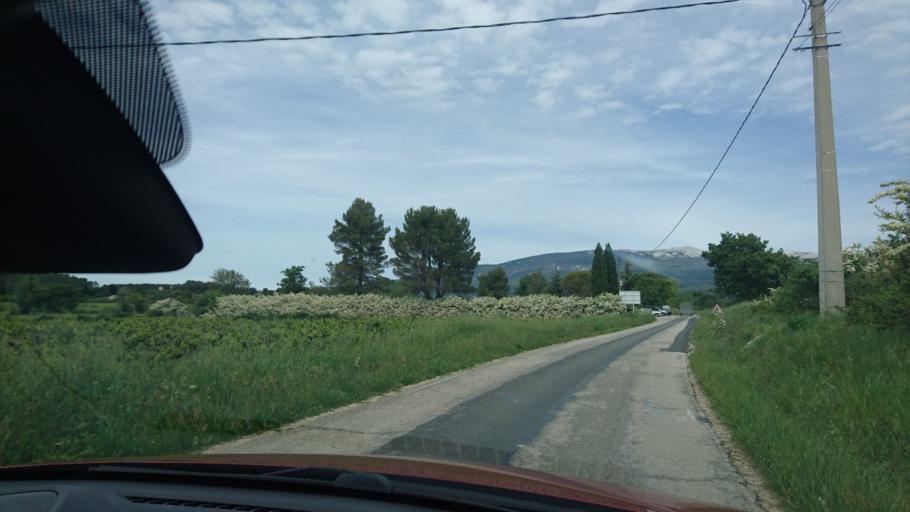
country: FR
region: Provence-Alpes-Cote d'Azur
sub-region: Departement du Vaucluse
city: Villes-sur-Auzon
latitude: 44.0737
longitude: 5.2338
